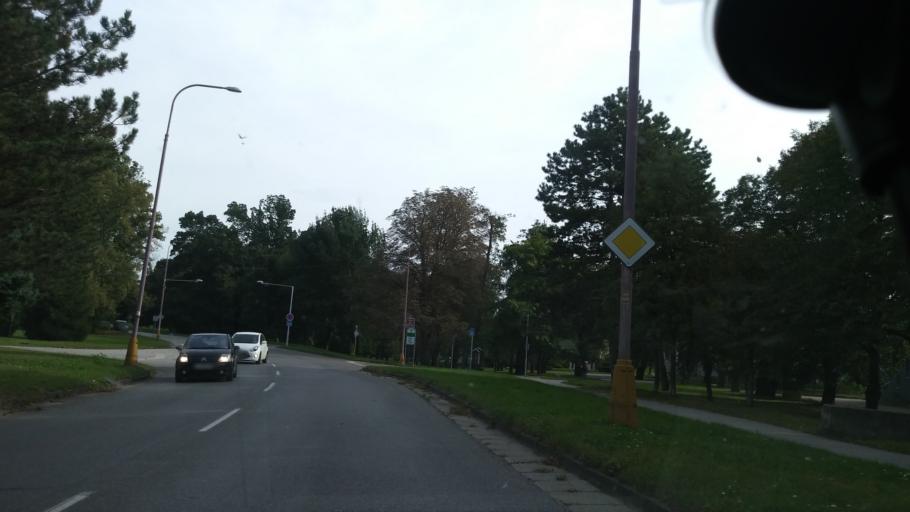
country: SK
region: Trnavsky
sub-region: Okres Skalica
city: Skalica
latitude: 48.8383
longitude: 17.2311
